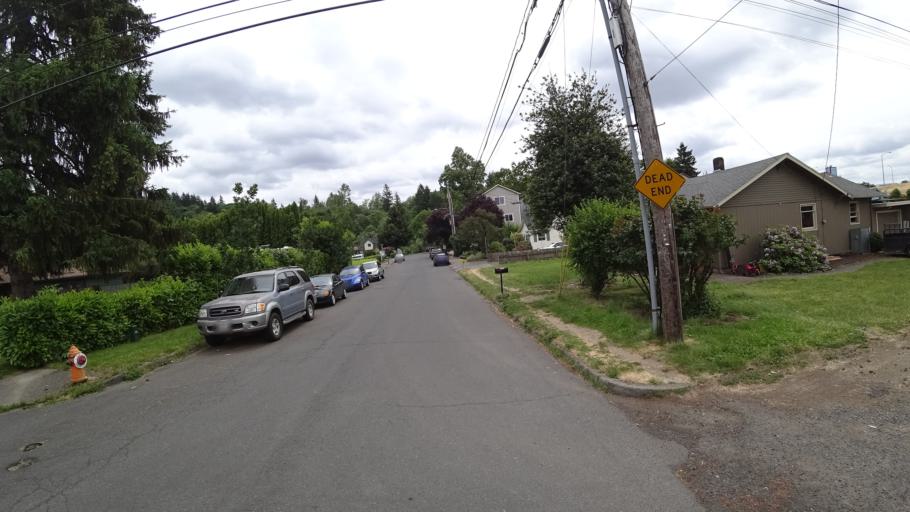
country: US
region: Oregon
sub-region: Multnomah County
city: Lents
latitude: 45.5028
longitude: -122.5628
